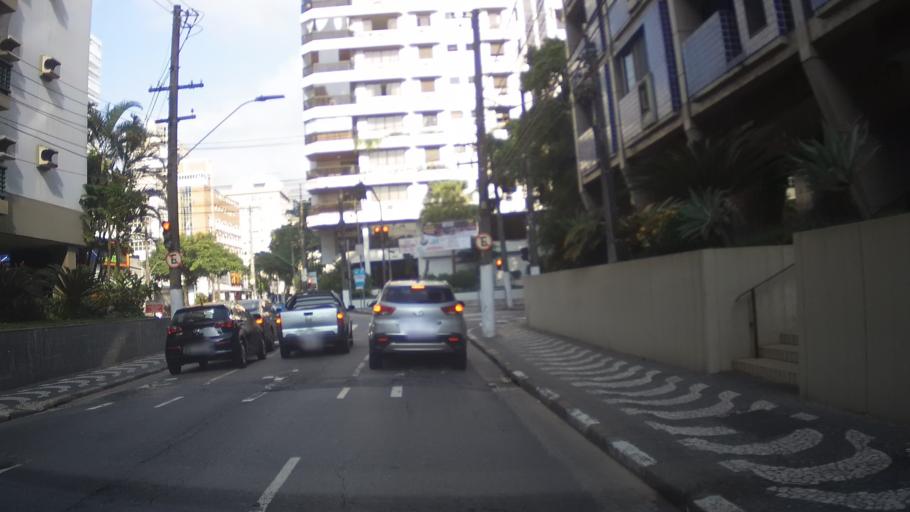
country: BR
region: Sao Paulo
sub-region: Santos
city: Santos
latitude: -23.9662
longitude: -46.3283
